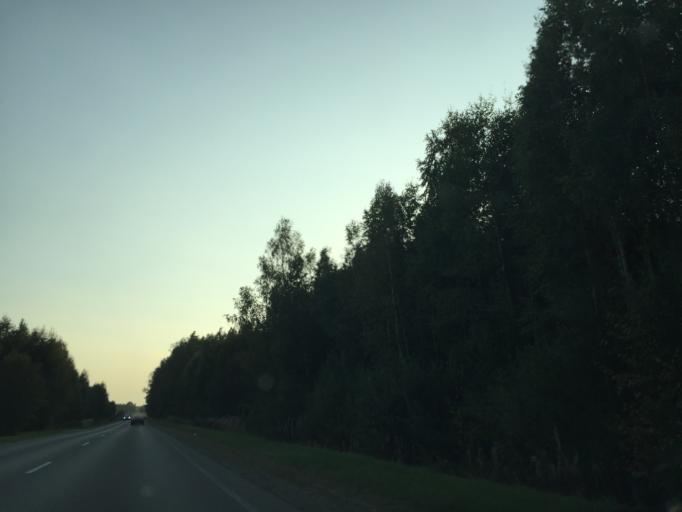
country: LV
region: Lielvarde
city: Lielvarde
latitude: 56.7822
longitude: 24.7917
